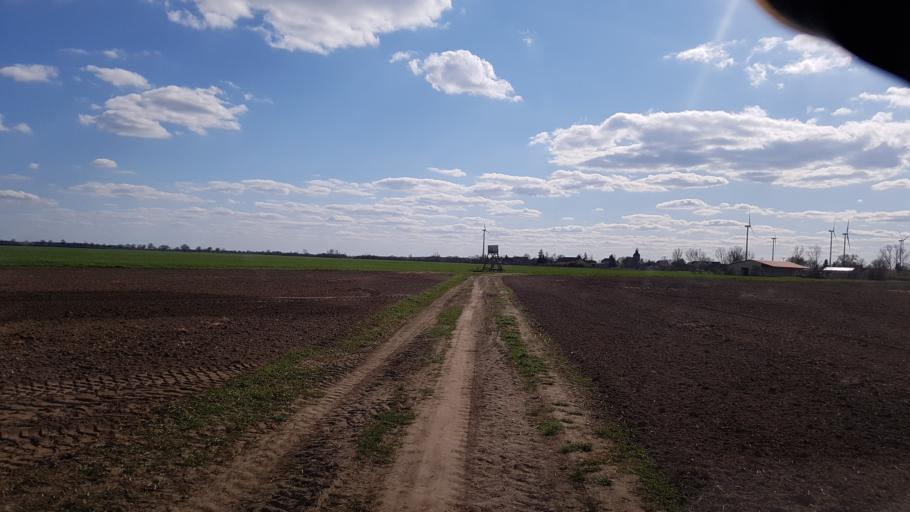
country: DE
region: Brandenburg
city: Muhlberg
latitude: 51.4777
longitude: 13.2772
